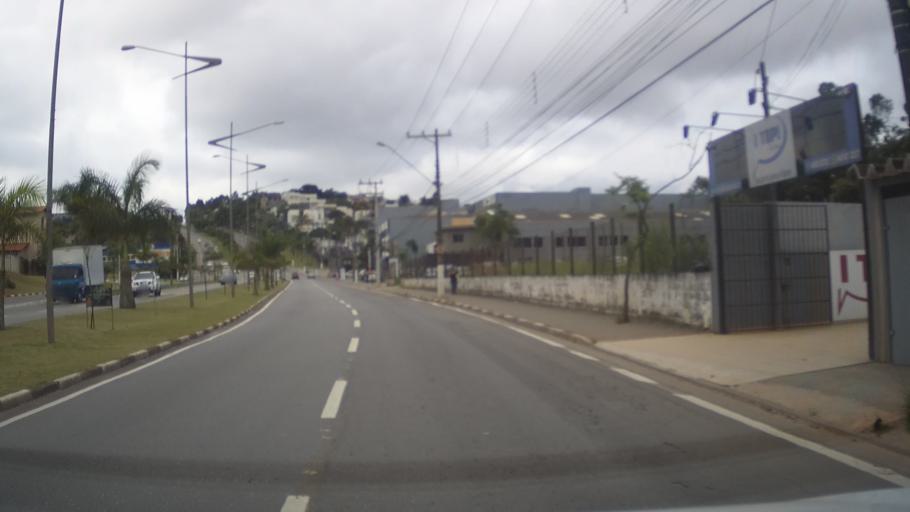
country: BR
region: Sao Paulo
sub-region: Aruja
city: Aruja
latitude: -23.4128
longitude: -46.3248
